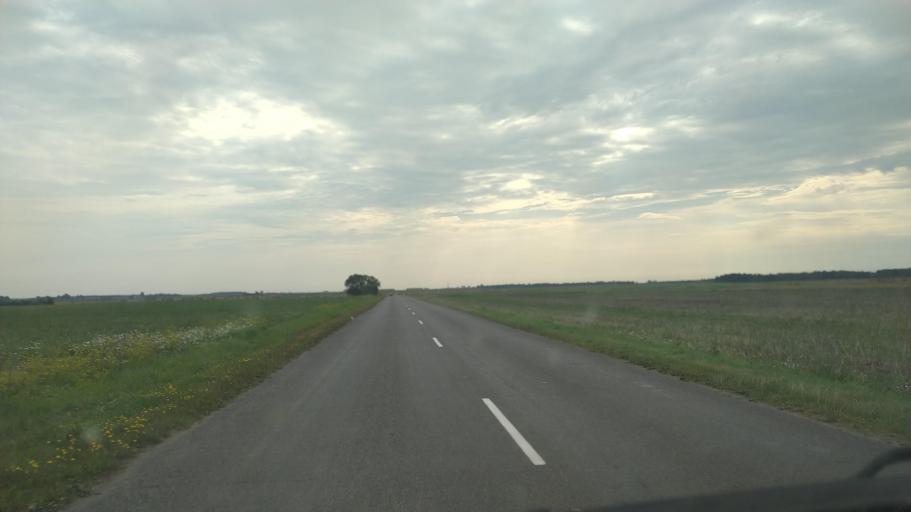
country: BY
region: Brest
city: Byaroza
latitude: 52.5767
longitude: 24.8647
